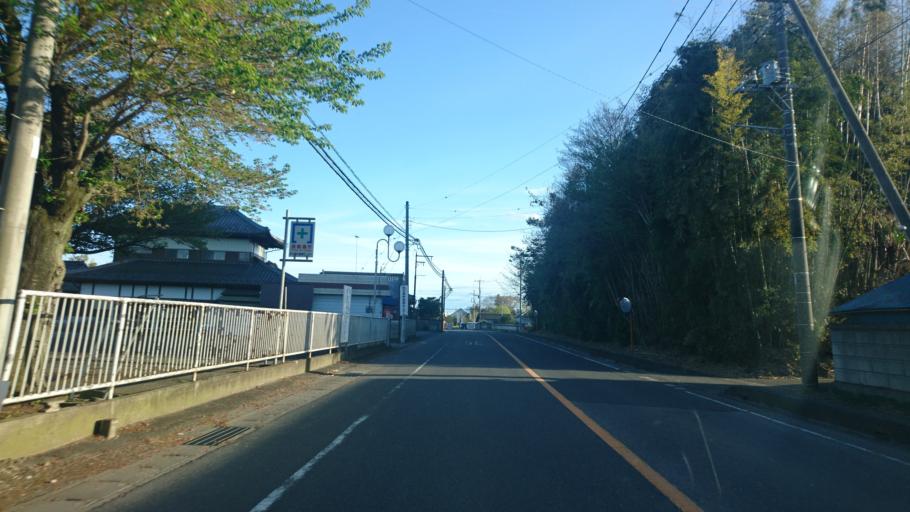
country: JP
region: Ibaraki
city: Shimodate
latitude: 36.2154
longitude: 139.9546
